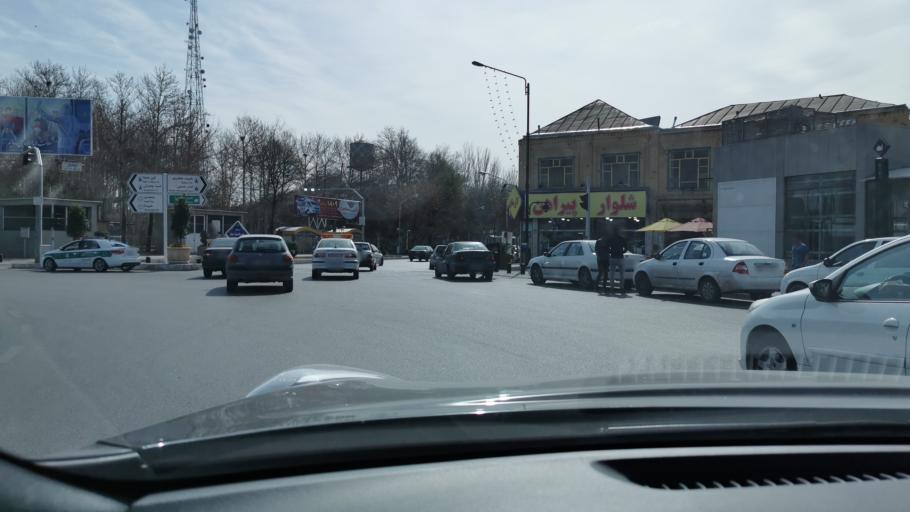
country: IR
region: Razavi Khorasan
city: Mashhad
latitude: 36.2909
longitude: 59.5859
